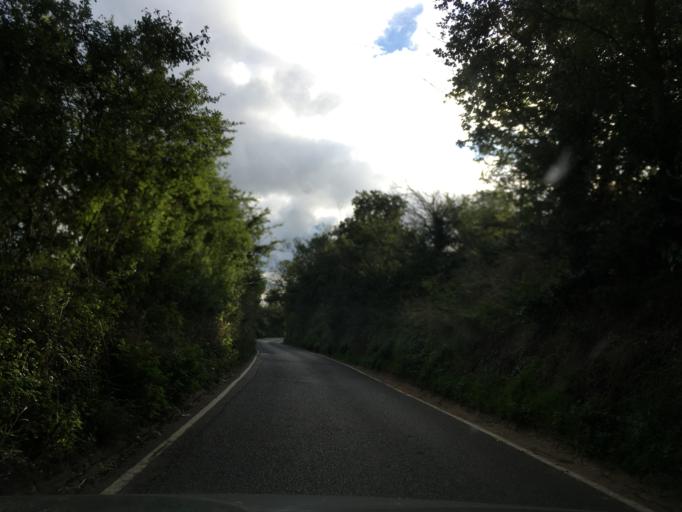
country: GB
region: England
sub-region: Kent
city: Herne Bay
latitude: 51.3714
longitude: 1.1823
